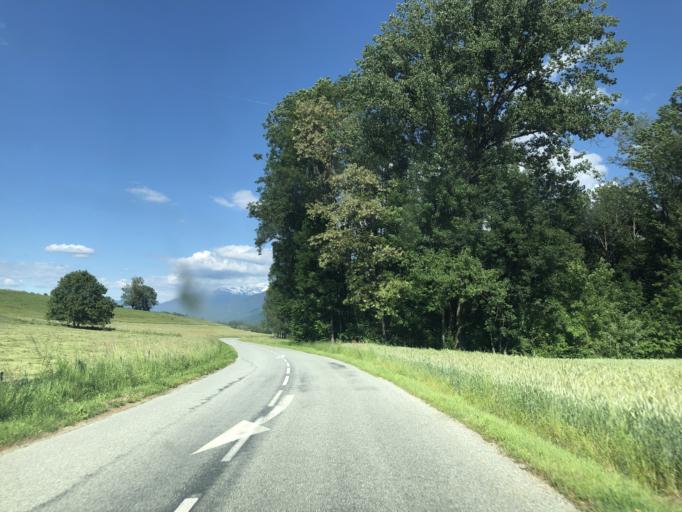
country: FR
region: Rhone-Alpes
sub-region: Departement de la Savoie
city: Coise-Saint-Jean-Pied-Gauthier
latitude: 45.5487
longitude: 6.1939
